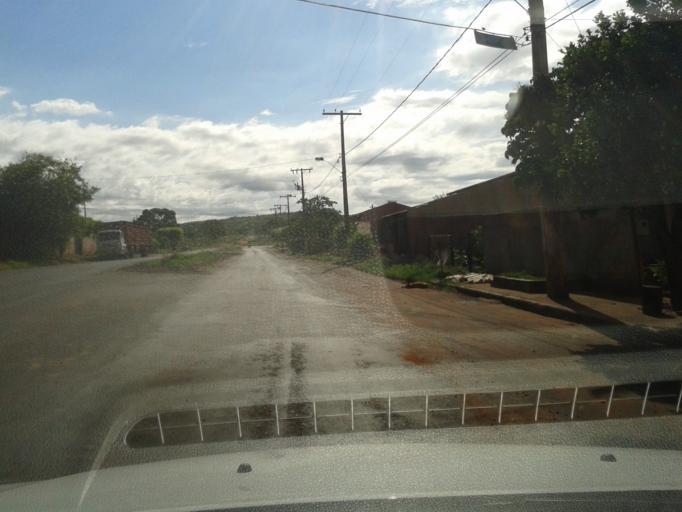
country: BR
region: Minas Gerais
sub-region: Ituiutaba
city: Ituiutaba
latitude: -19.2126
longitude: -49.7799
